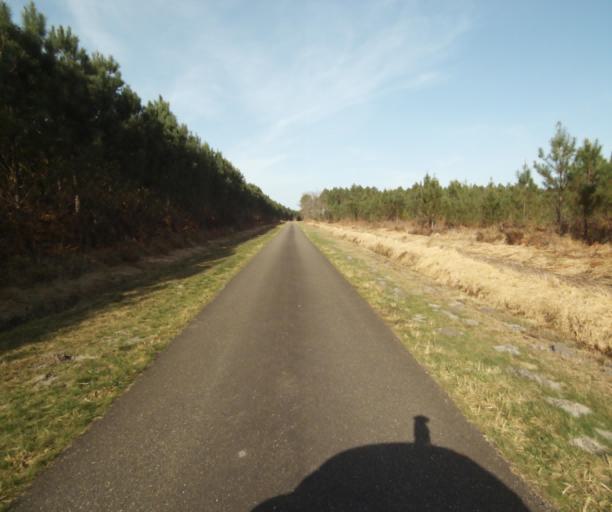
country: FR
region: Aquitaine
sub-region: Departement des Landes
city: Sarbazan
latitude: 44.1303
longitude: -0.1595
